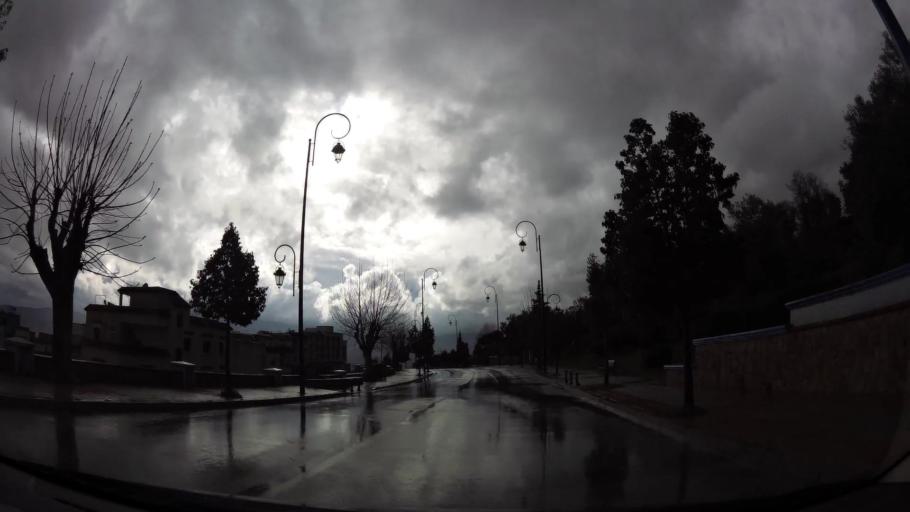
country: MA
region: Tanger-Tetouan
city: Chefchaouene
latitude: 35.1726
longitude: -5.2747
